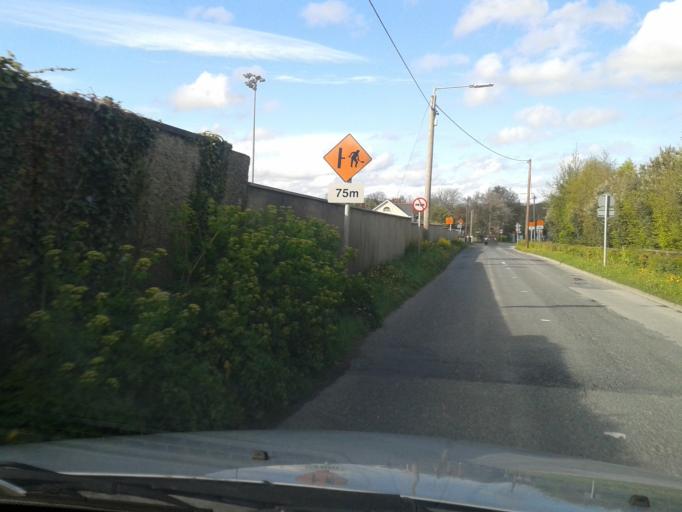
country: IE
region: Leinster
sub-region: Fingal County
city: Swords
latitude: 53.4669
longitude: -6.2119
